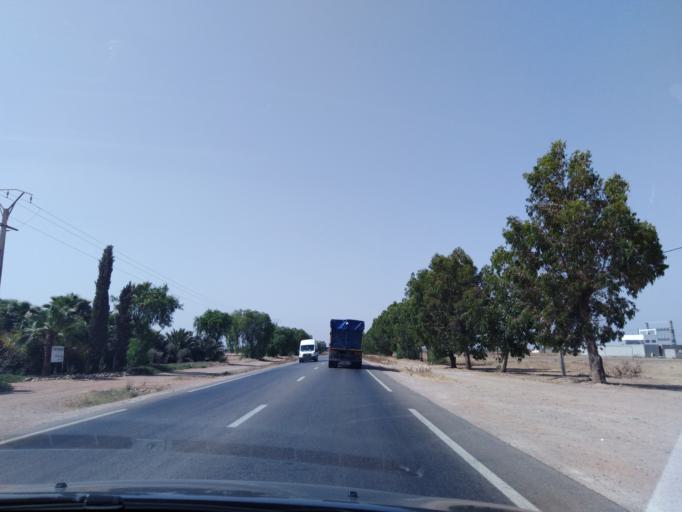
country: MA
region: Chaouia-Ouardigha
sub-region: Settat Province
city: Berrechid
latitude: 33.1946
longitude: -7.6140
